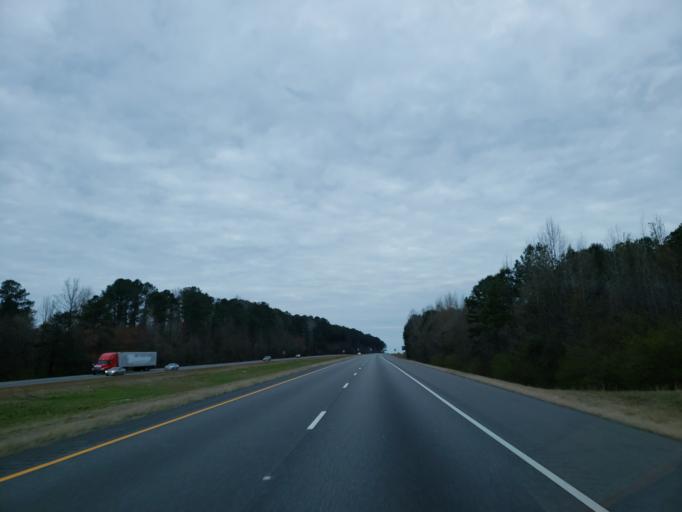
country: US
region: Alabama
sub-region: Hale County
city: Moundville
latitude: 32.9932
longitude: -87.7794
